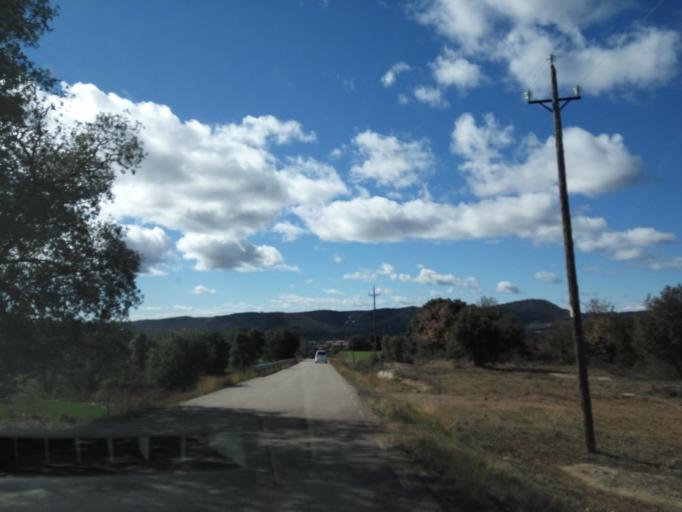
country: ES
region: Catalonia
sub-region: Provincia de Barcelona
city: Capolat
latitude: 42.0220
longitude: 1.7721
